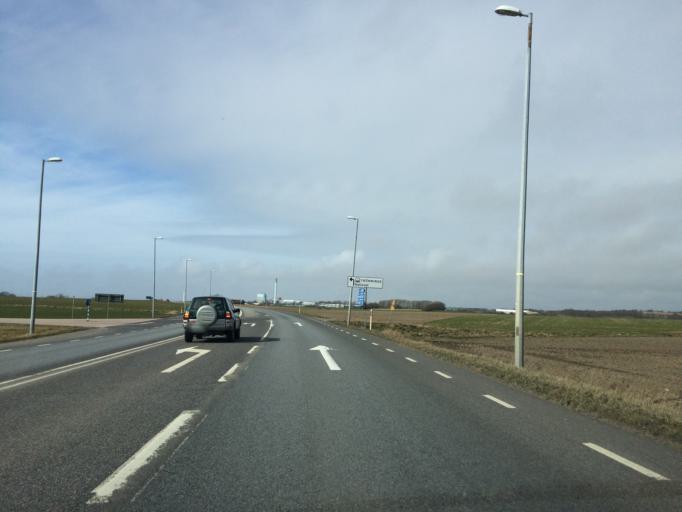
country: SE
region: Halland
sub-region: Halmstads Kommun
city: Troenninge
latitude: 56.6220
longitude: 12.9541
